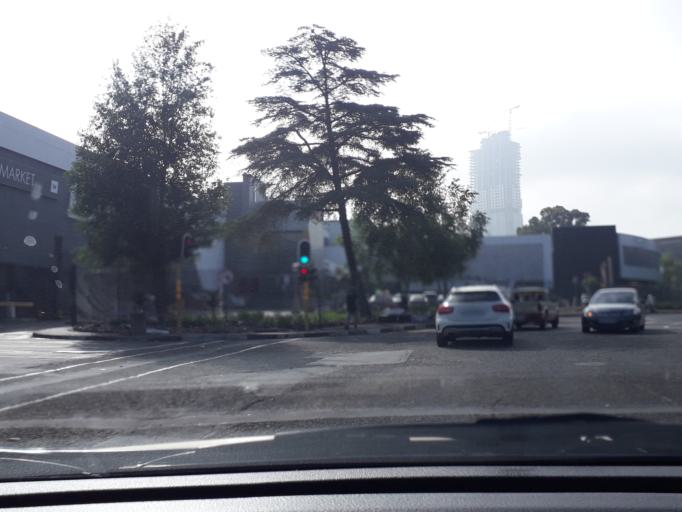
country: ZA
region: Gauteng
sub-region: City of Johannesburg Metropolitan Municipality
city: Johannesburg
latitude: -26.0999
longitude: 28.0477
